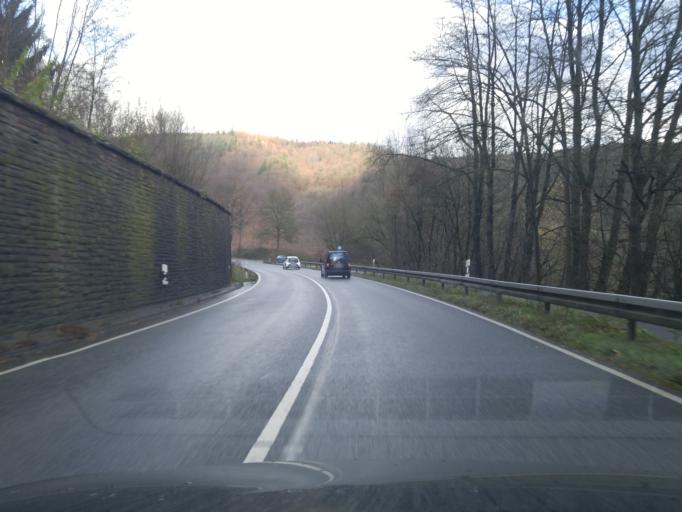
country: DE
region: Lower Saxony
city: Buhren
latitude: 51.4655
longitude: 9.6396
